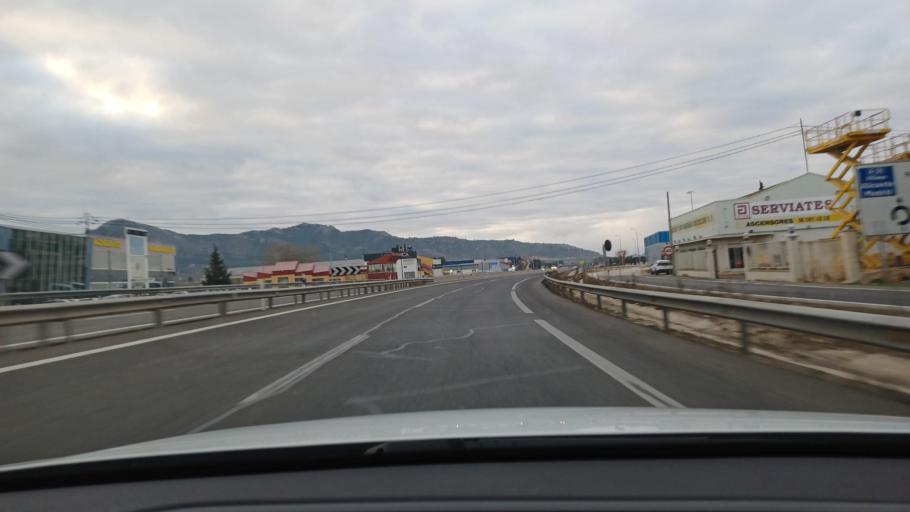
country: ES
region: Valencia
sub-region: Provincia de Alicante
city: Villena
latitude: 38.6172
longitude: -0.8480
